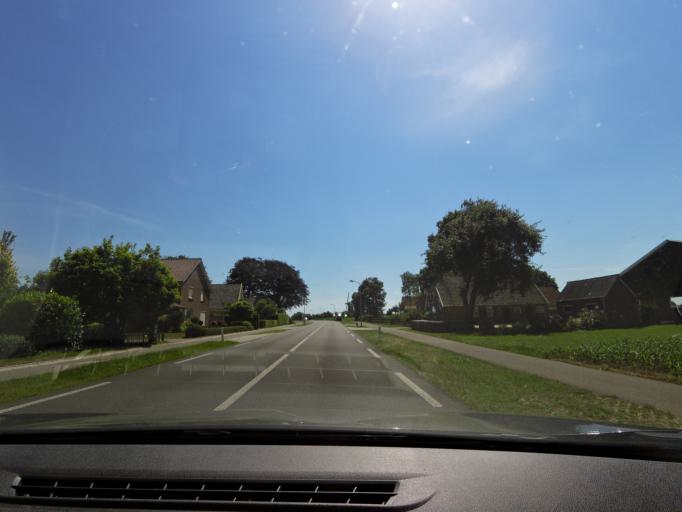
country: NL
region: Gelderland
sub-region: Berkelland
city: Neede
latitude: 52.1451
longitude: 6.6113
